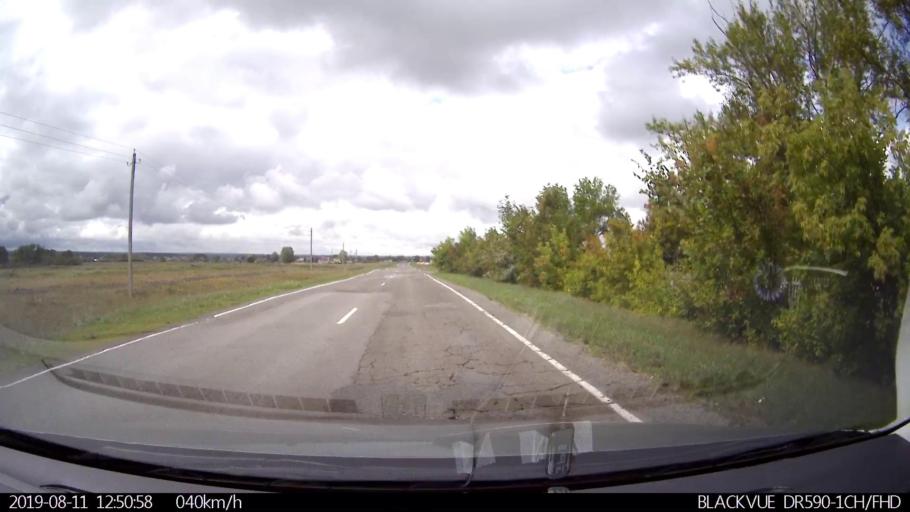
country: RU
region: Ulyanovsk
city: Ignatovka
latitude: 53.8755
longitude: 47.6668
